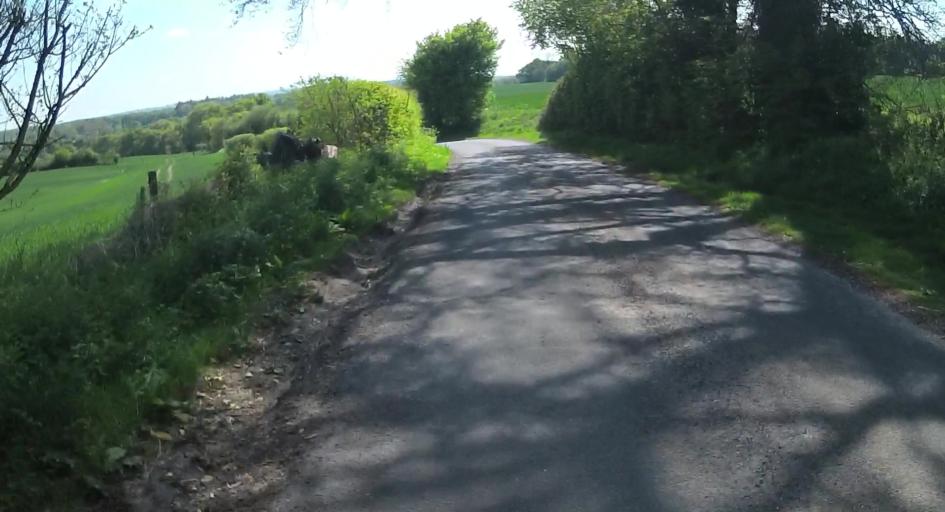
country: GB
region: England
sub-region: Hampshire
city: Four Marks
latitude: 51.1242
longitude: -1.0951
